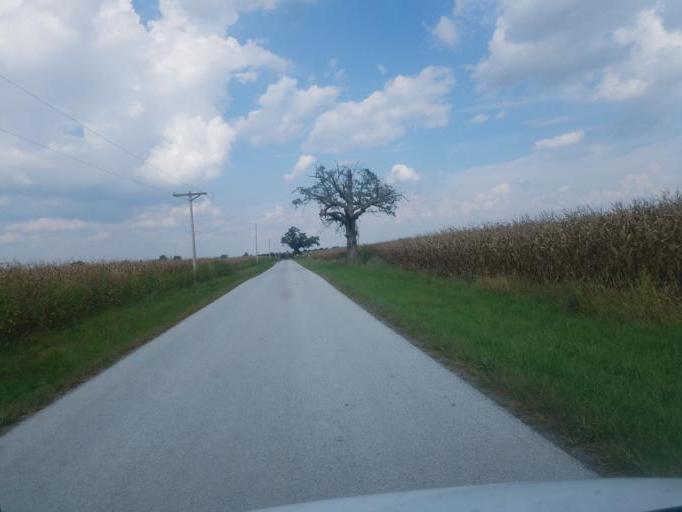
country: US
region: Ohio
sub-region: Hardin County
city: Kenton
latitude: 40.6319
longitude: -83.6529
